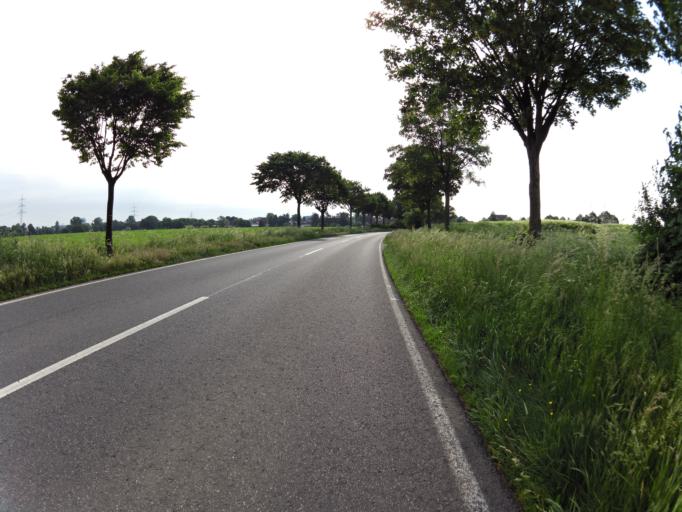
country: DE
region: North Rhine-Westphalia
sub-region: Regierungsbezirk Koln
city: Aldenhoven
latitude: 50.9334
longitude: 6.2845
